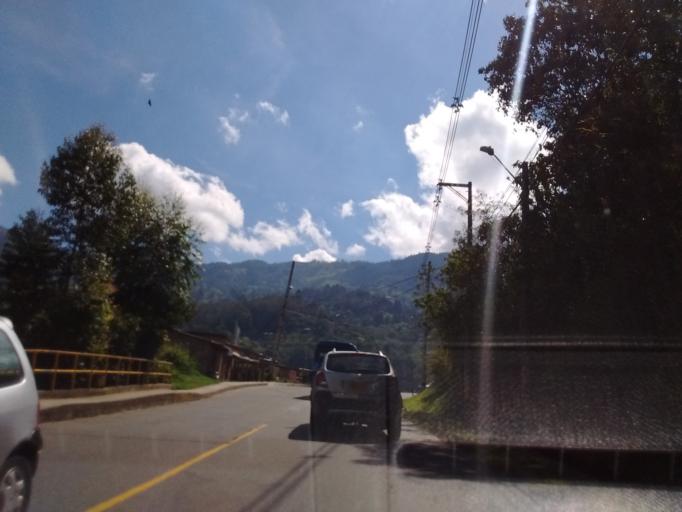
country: CO
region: Antioquia
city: Medellin
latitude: 6.2279
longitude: -75.5258
